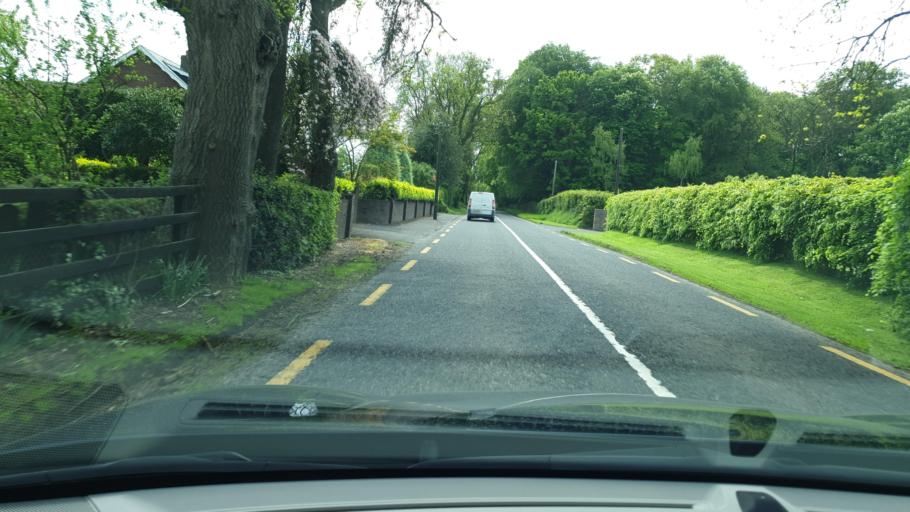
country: IE
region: Ulster
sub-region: An Cabhan
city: Kingscourt
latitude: 53.8443
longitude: -6.7735
